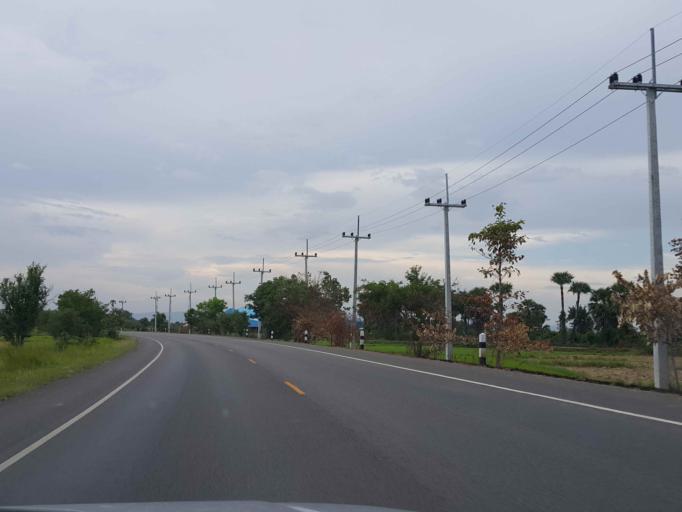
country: TH
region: Lampang
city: Ko Kha
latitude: 18.2243
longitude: 99.3960
